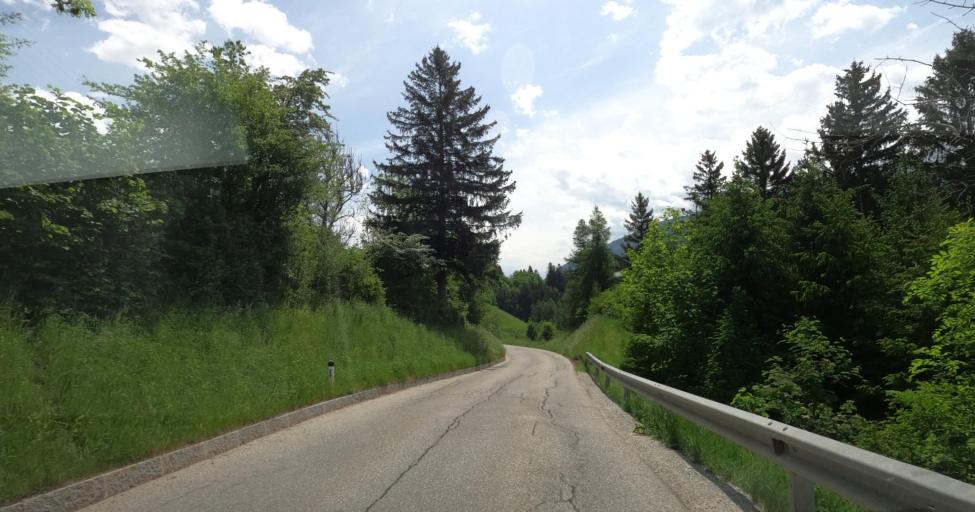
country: AT
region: Tyrol
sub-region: Politischer Bezirk Innsbruck Land
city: Schoenberg im Stubaital
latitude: 47.1907
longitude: 11.4276
